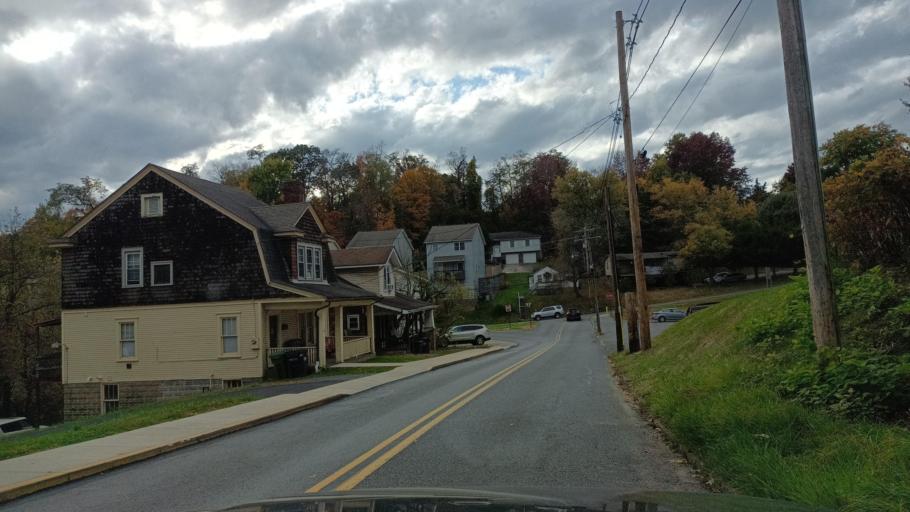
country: US
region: West Virginia
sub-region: Monongalia County
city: Morgantown
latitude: 39.6421
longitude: -79.9490
